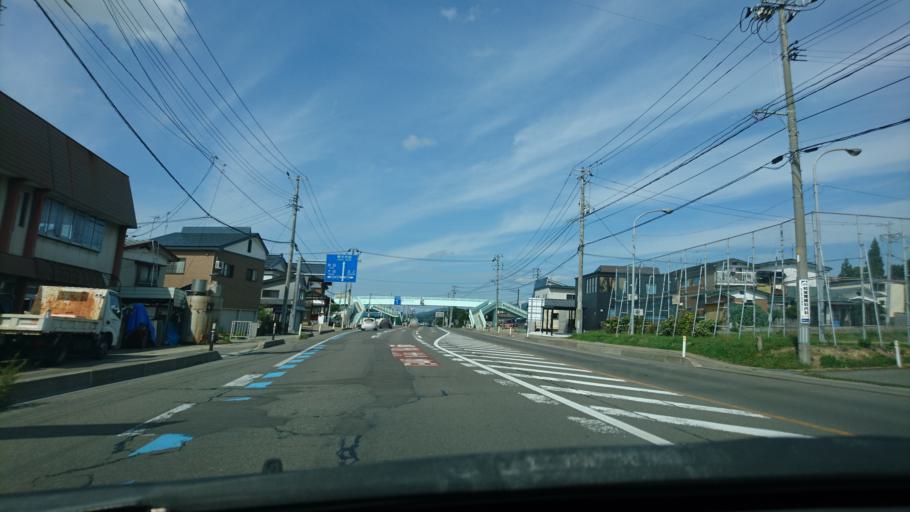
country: JP
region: Akita
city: Yokotemachi
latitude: 39.2976
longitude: 140.5638
